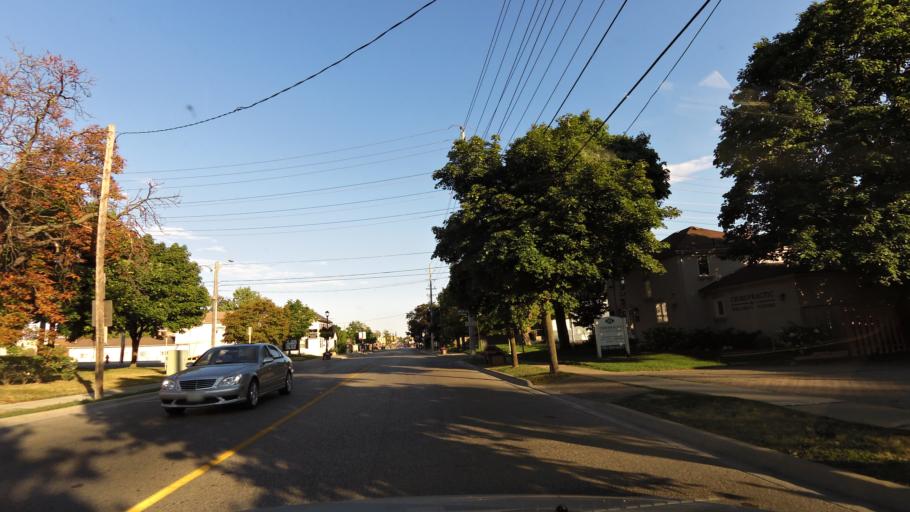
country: CA
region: Ontario
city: Mississauga
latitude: 43.5852
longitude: -79.7185
